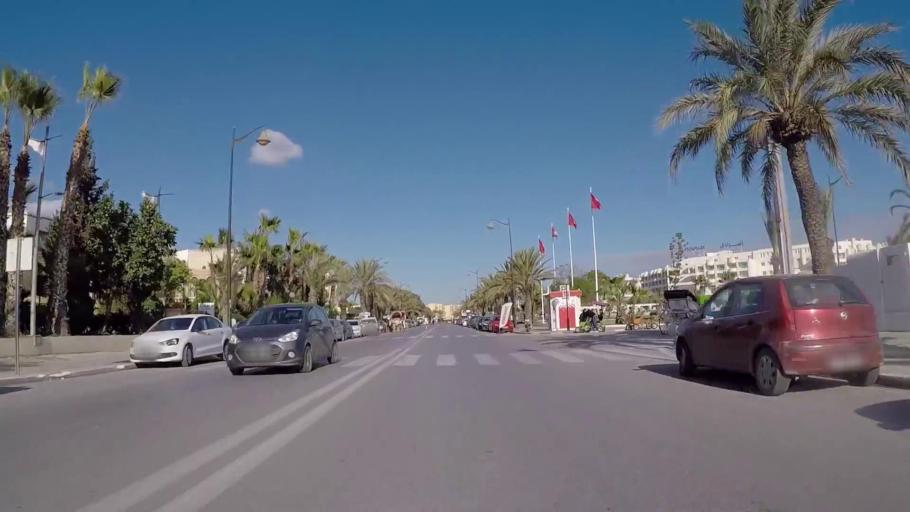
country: TN
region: Nabul
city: Al Hammamat
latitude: 36.3650
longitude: 10.5333
